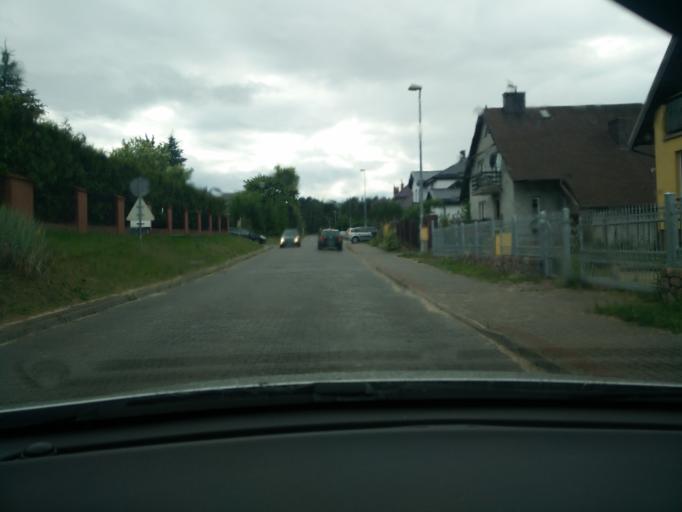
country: PL
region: Pomeranian Voivodeship
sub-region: Powiat pucki
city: Mosty
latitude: 54.6058
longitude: 18.4901
